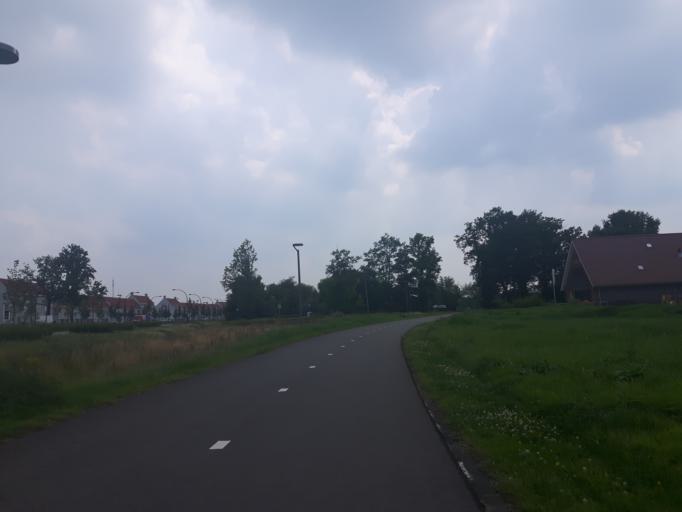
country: NL
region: Overijssel
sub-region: Gemeente Borne
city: Borne
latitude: 52.3000
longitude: 6.7716
